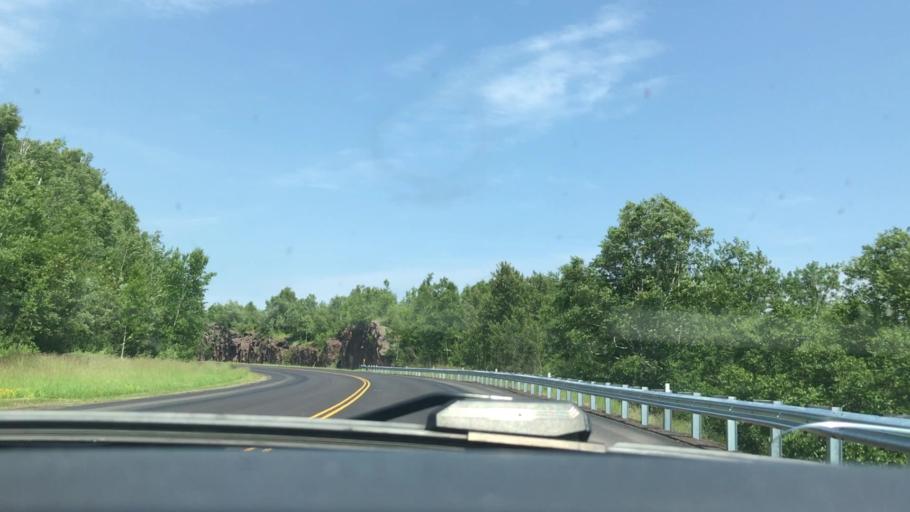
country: US
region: Minnesota
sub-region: Lake County
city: Silver Bay
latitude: 47.3682
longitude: -91.1686
